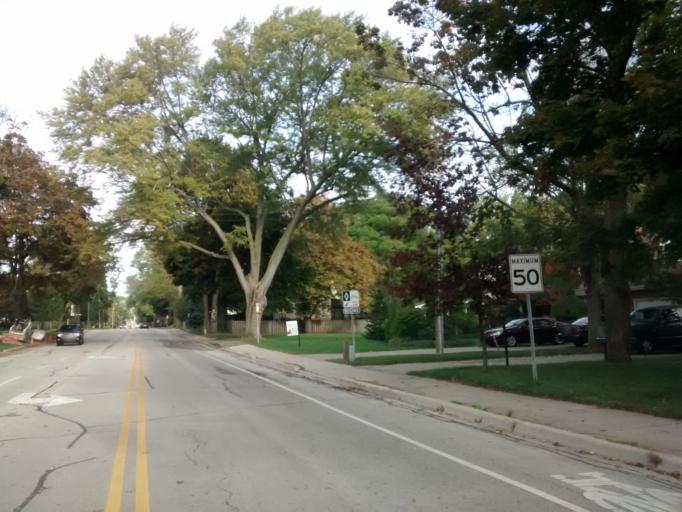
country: CA
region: Ontario
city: Burlington
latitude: 43.3332
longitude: -79.7783
